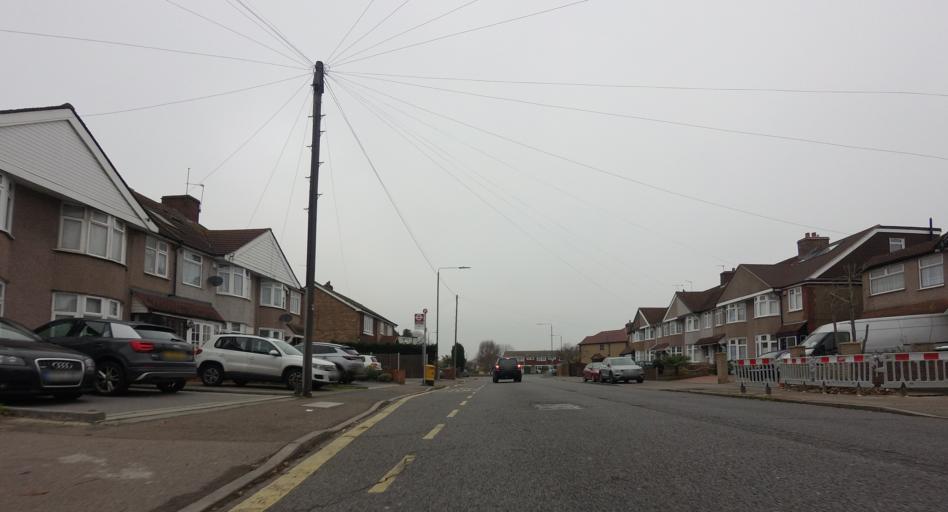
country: GB
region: England
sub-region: Greater London
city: Sidcup
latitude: 51.4387
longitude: 0.1188
